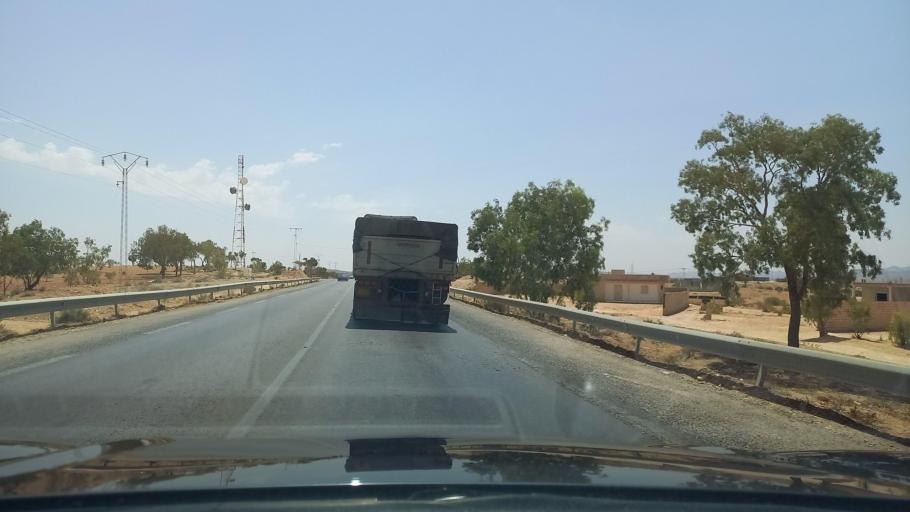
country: TN
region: Madanin
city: Medenine
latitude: 33.5710
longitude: 10.3171
